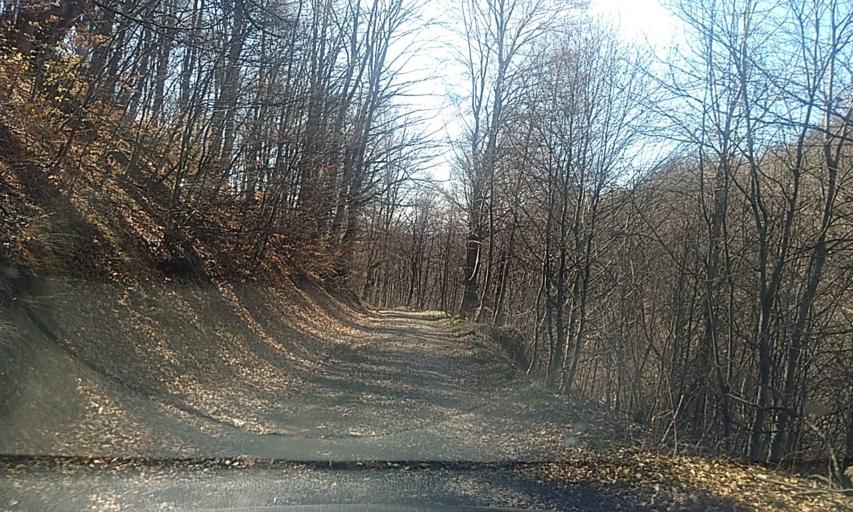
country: RS
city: Radovnica
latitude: 42.3530
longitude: 22.3368
